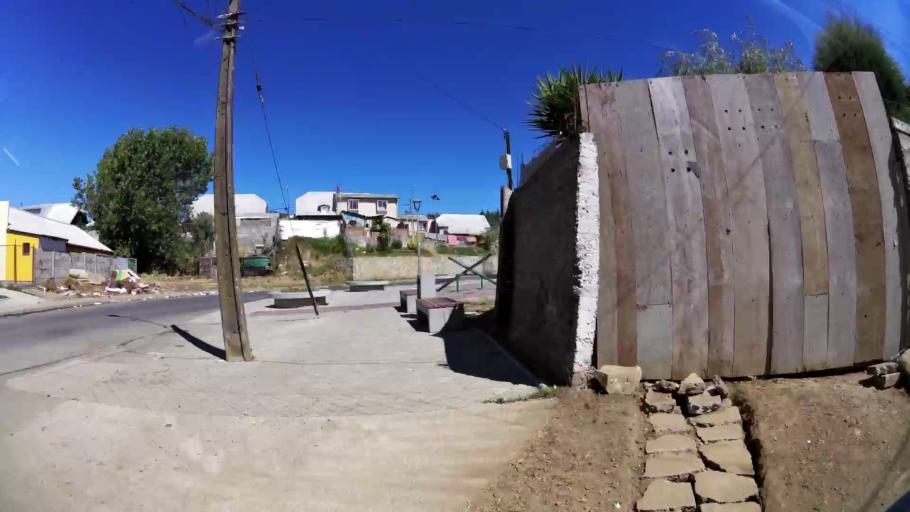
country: CL
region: Biobio
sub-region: Provincia de Concepcion
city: Penco
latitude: -36.7281
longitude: -72.9824
